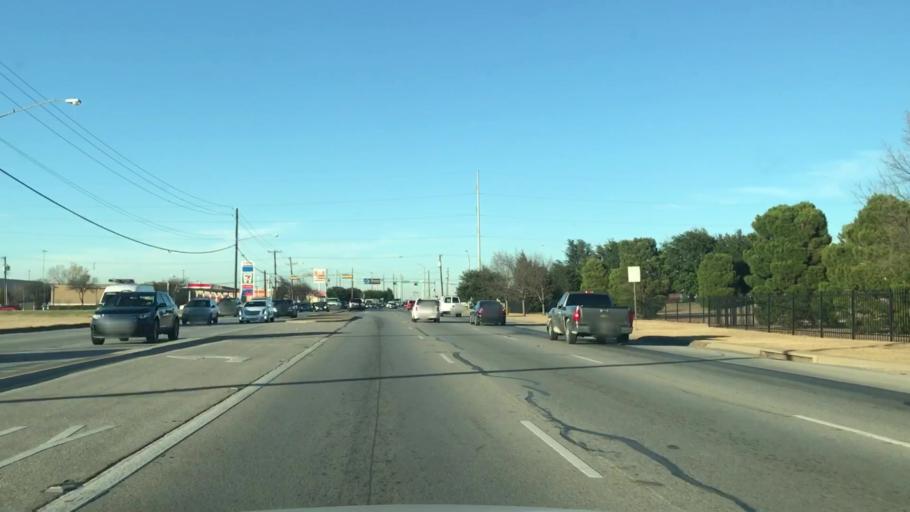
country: US
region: Texas
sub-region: Dallas County
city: Balch Springs
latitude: 32.7909
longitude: -96.6850
